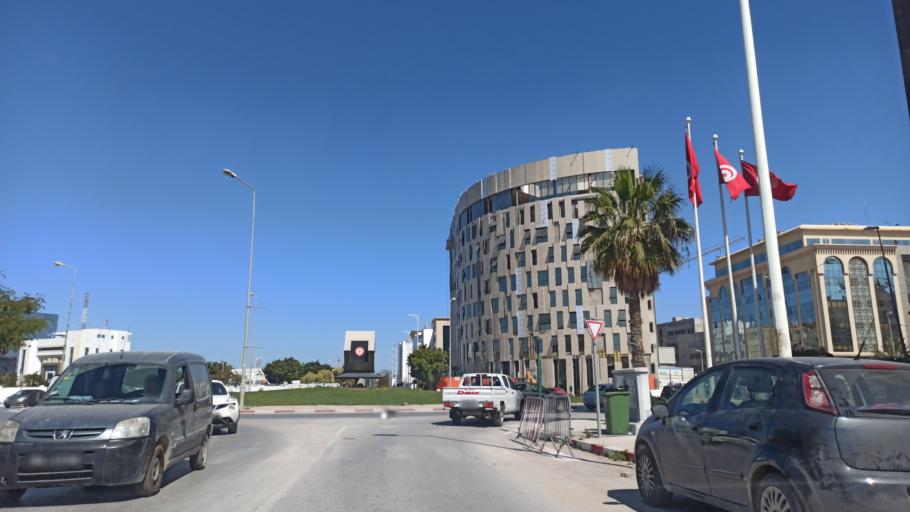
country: TN
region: Ariana
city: Ariana
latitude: 36.8414
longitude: 10.1982
